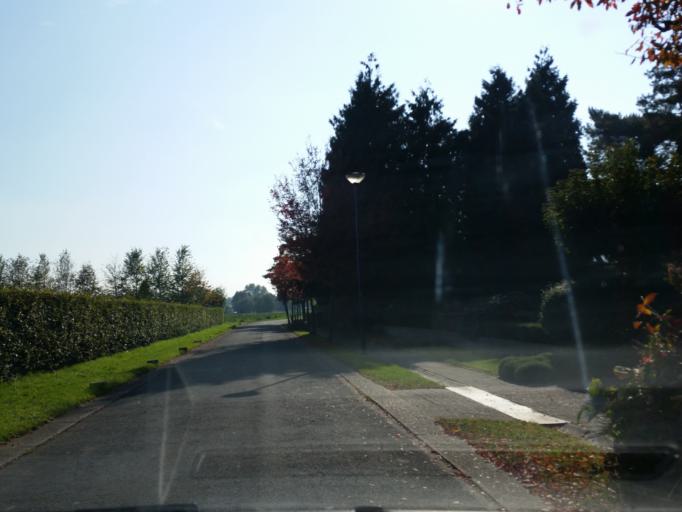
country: BE
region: Flanders
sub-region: Provincie Antwerpen
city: Kontich
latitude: 51.1099
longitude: 4.4388
